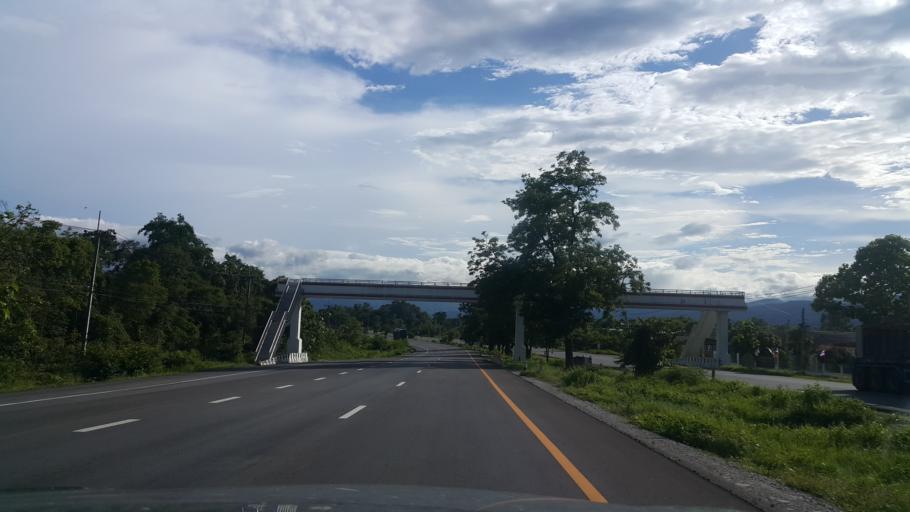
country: TH
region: Tak
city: Ban Tak
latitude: 17.1352
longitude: 99.1078
